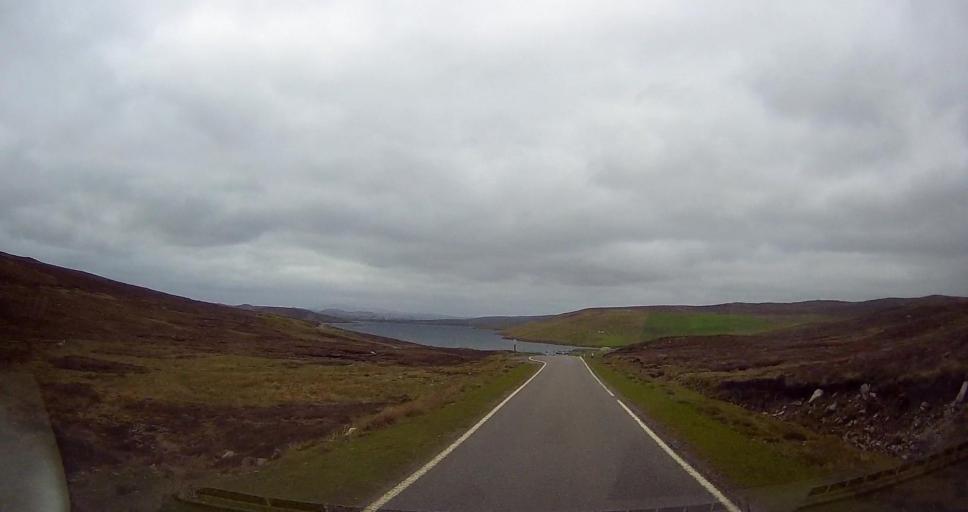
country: GB
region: Scotland
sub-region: Shetland Islands
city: Lerwick
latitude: 60.3265
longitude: -1.3387
